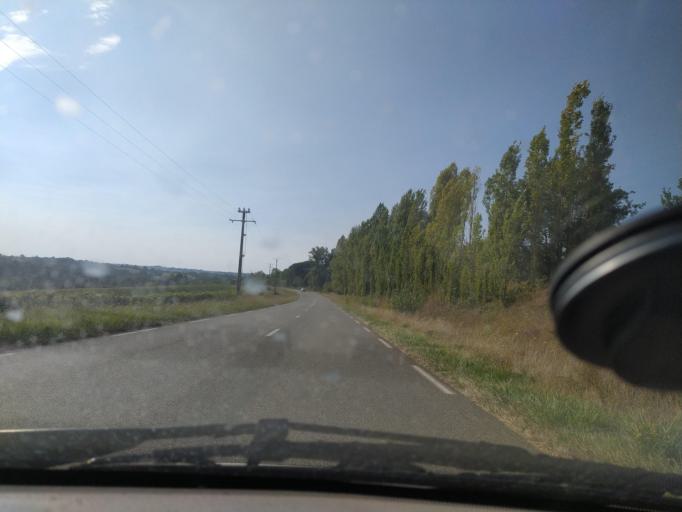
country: FR
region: Midi-Pyrenees
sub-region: Departement du Gers
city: Eauze
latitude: 43.7965
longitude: 0.0746
